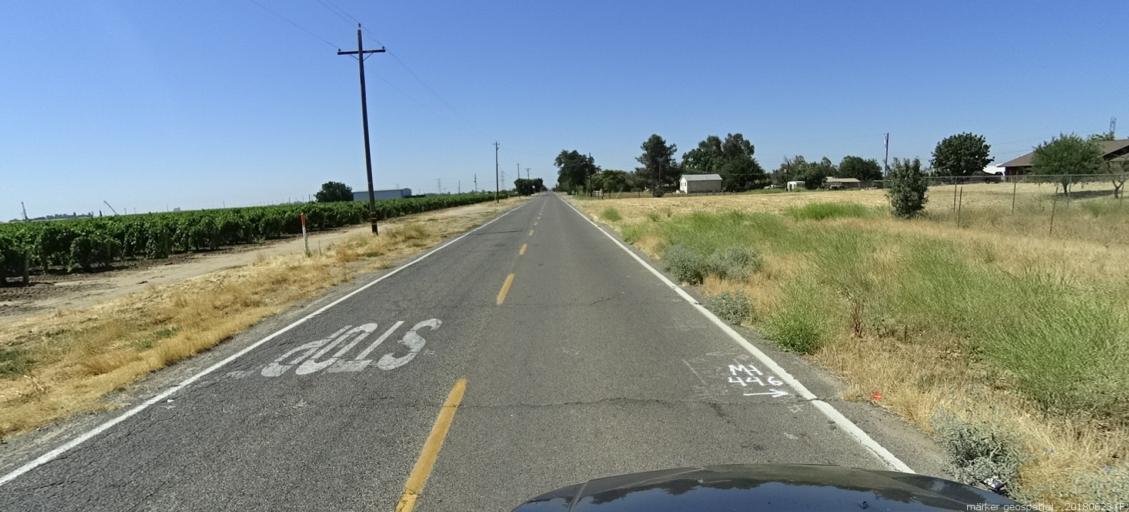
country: US
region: California
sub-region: Madera County
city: Parksdale
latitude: 36.9727
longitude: -120.0197
